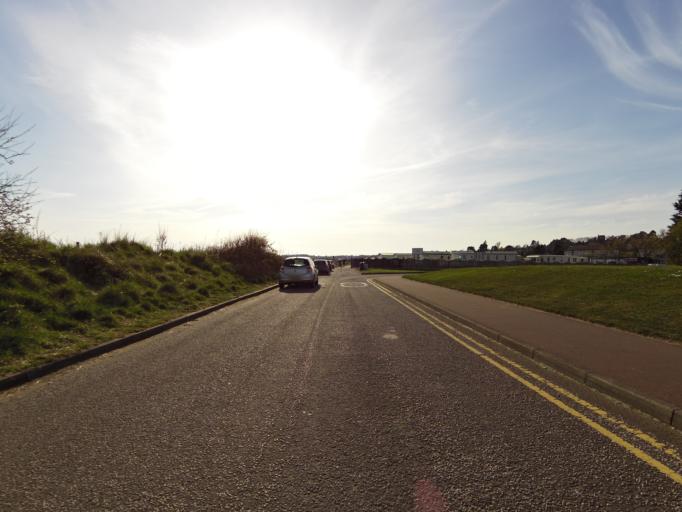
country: GB
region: Scotland
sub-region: Fife
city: Tayport
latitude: 56.4786
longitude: -2.8158
